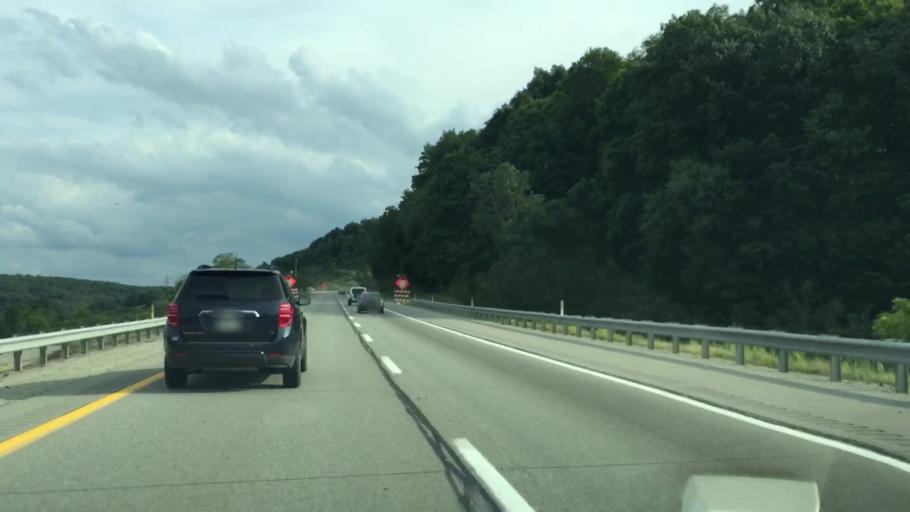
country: US
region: Pennsylvania
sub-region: Allegheny County
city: Ben Avon
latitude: 40.5420
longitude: -80.0817
